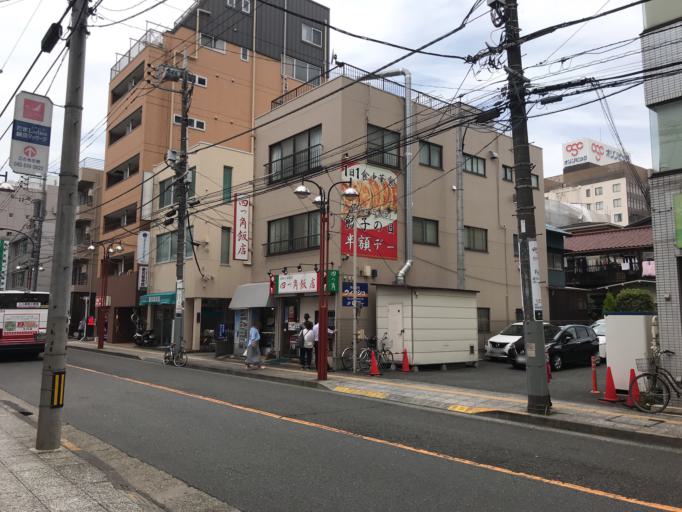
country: JP
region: Tokyo
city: Hino
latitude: 35.6987
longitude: 139.4102
